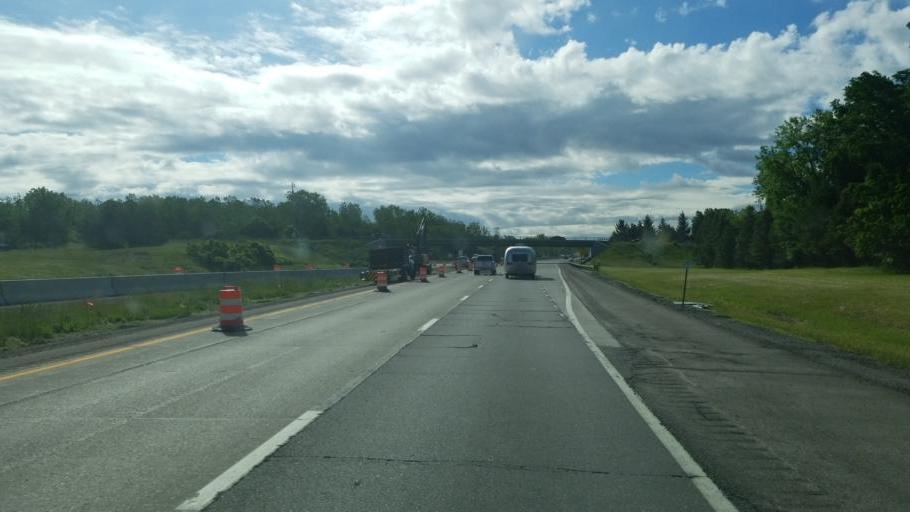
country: US
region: New York
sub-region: Ontario County
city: Victor
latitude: 43.0098
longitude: -77.4416
